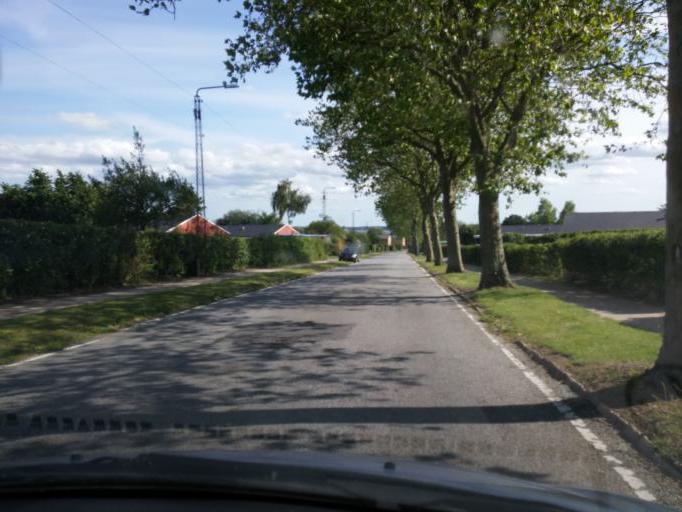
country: DK
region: South Denmark
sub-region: Kerteminde Kommune
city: Munkebo
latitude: 55.4634
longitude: 10.5562
